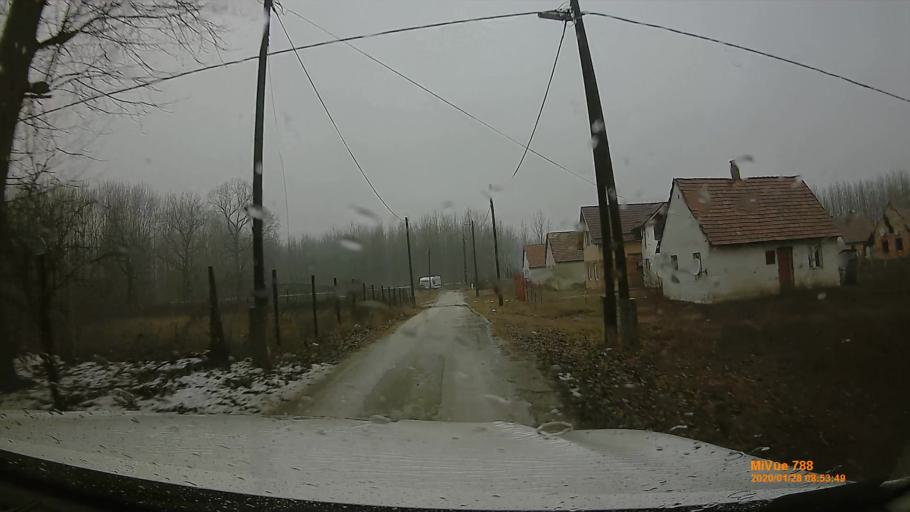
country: HU
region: Pest
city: Pilis
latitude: 47.2987
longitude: 19.5341
